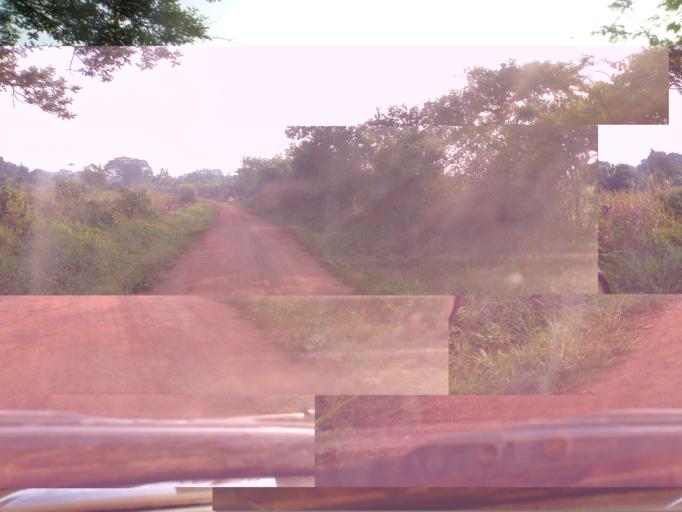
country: UG
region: Western Region
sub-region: Masindi District
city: Masindi
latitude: 1.7656
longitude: 31.8389
